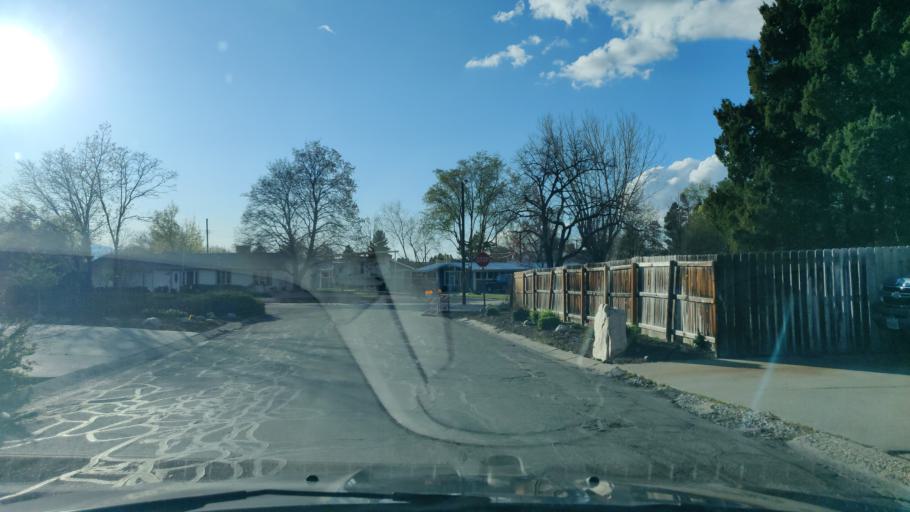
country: US
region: Utah
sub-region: Salt Lake County
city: Cottonwood Heights
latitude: 40.6230
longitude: -111.8088
